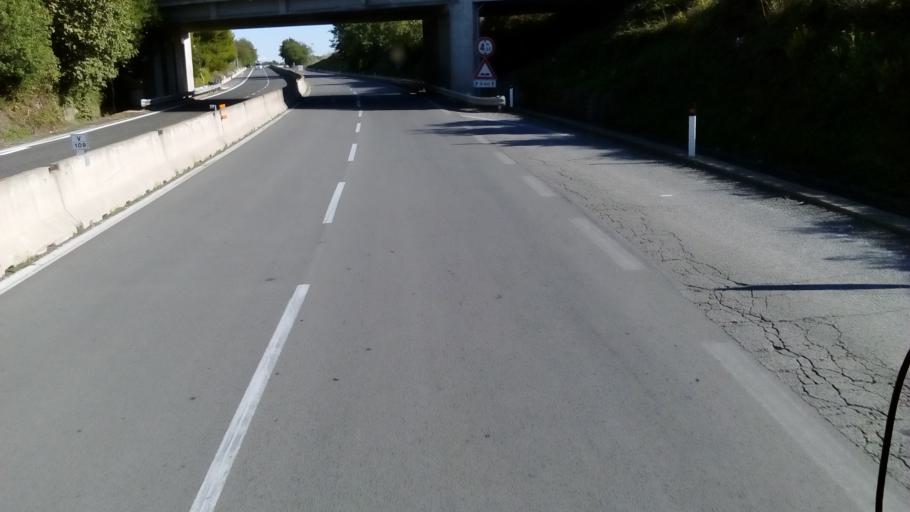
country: IT
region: Latium
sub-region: Provincia di Viterbo
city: Montalto di Castro
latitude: 42.3478
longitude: 11.6040
